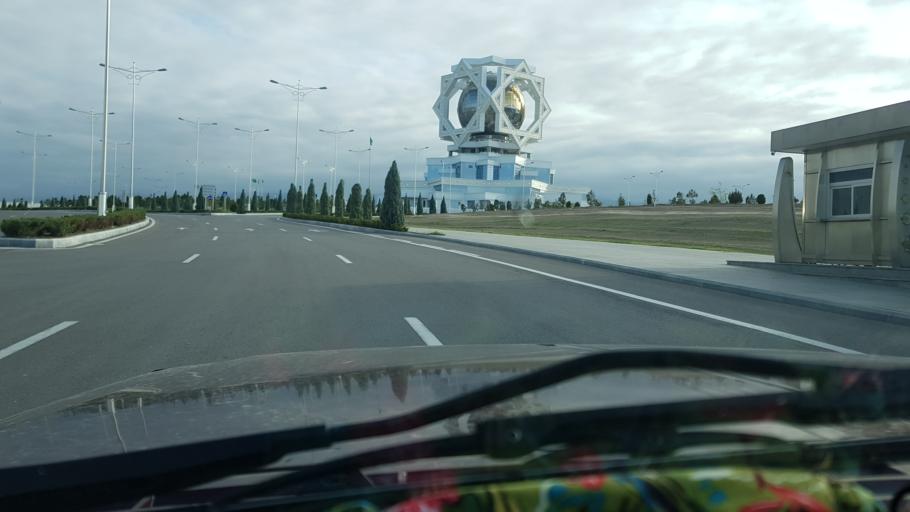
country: TM
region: Ahal
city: Ashgabat
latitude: 37.9295
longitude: 58.3433
